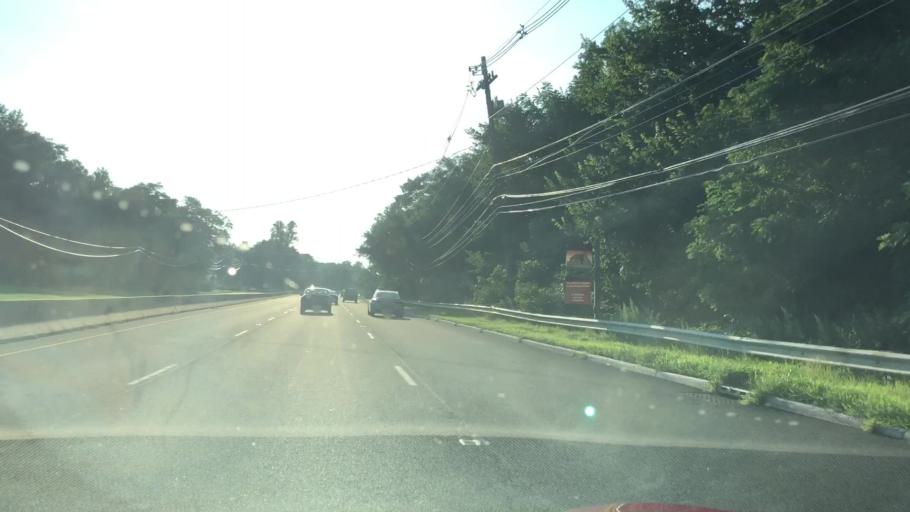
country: US
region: New Jersey
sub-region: Morris County
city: Morris Plains
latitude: 40.8555
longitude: -74.4806
